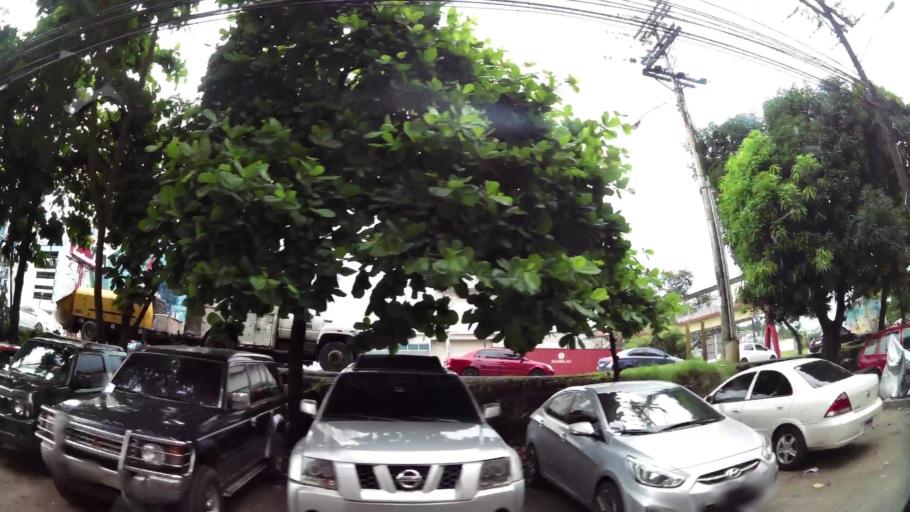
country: PA
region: Panama
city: Panama
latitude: 9.0259
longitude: -79.5212
